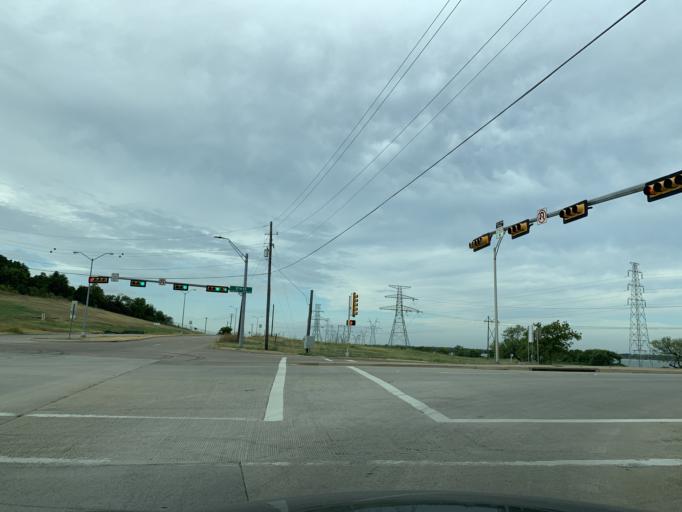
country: US
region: Texas
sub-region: Dallas County
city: Grand Prairie
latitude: 32.7074
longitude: -96.9525
